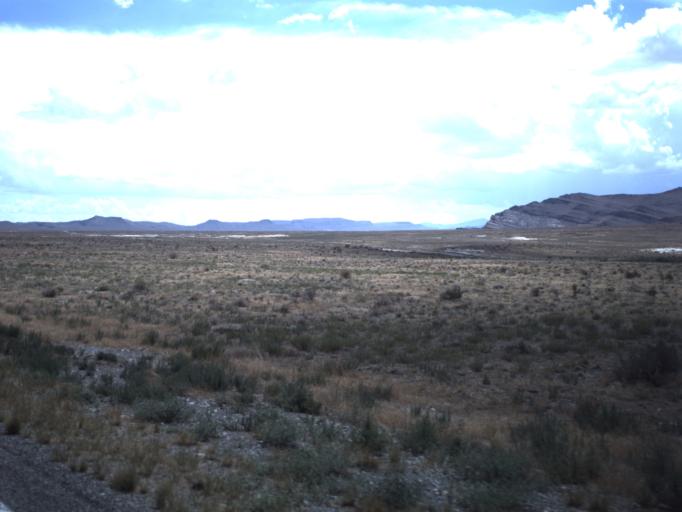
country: US
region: Utah
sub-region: Beaver County
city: Milford
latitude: 39.0395
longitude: -113.3988
